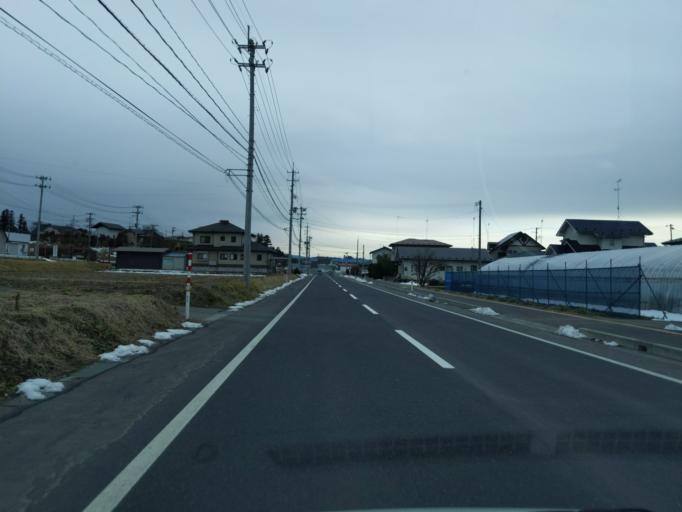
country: JP
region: Iwate
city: Mizusawa
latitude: 39.1828
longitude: 141.1894
